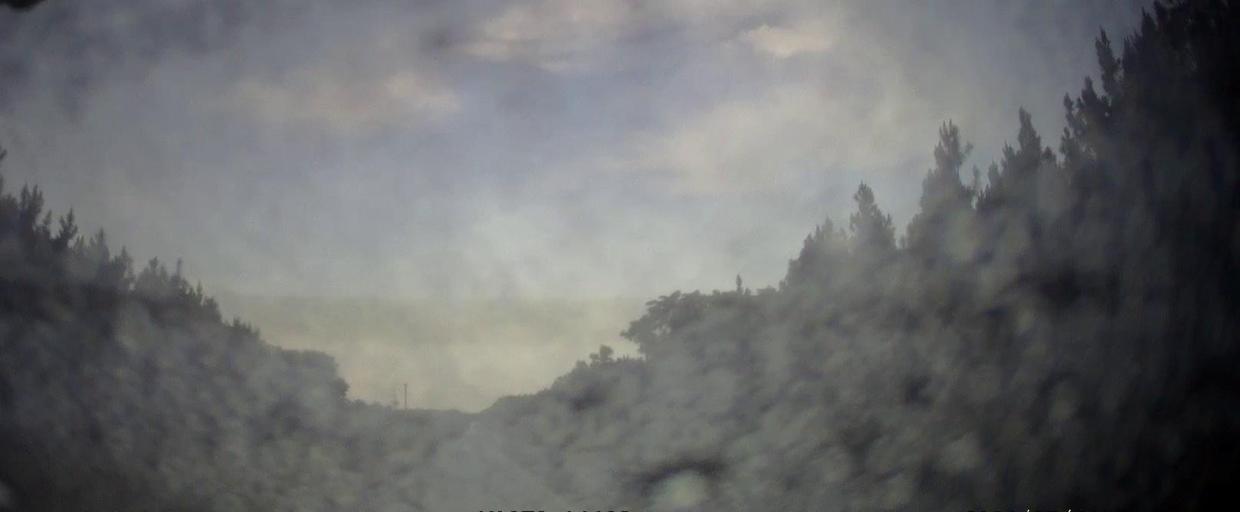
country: US
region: Georgia
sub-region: Dodge County
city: Chester
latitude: 32.5499
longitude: -83.1297
